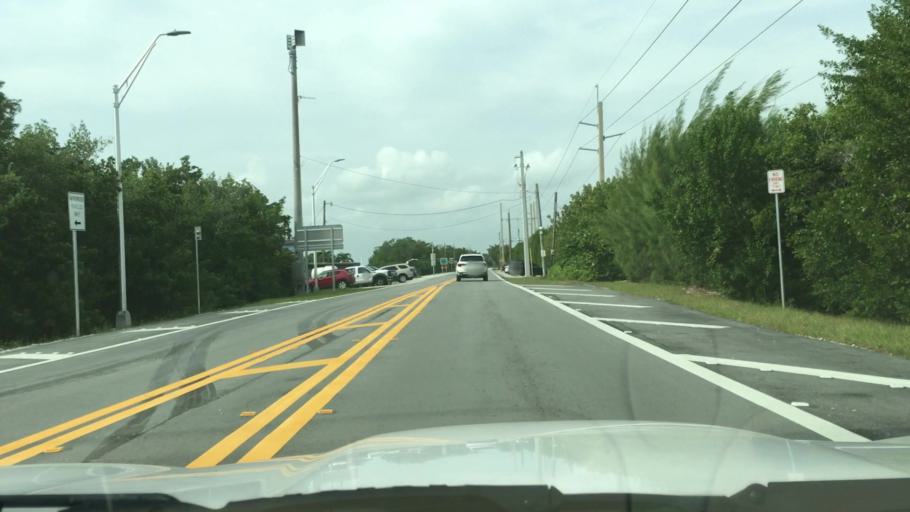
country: US
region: Florida
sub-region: Monroe County
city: North Key Largo
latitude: 25.2912
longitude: -80.3779
